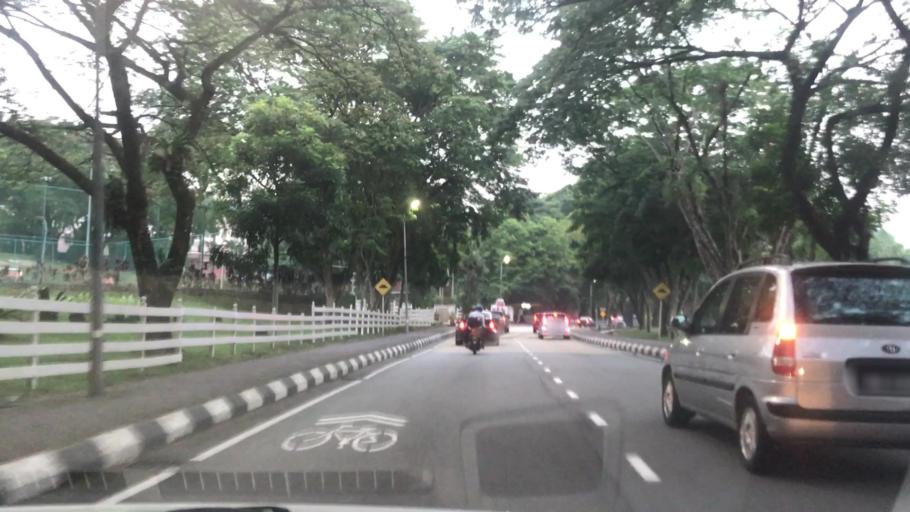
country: MY
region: Kuala Lumpur
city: Kuala Lumpur
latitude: 3.1185
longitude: 101.6603
